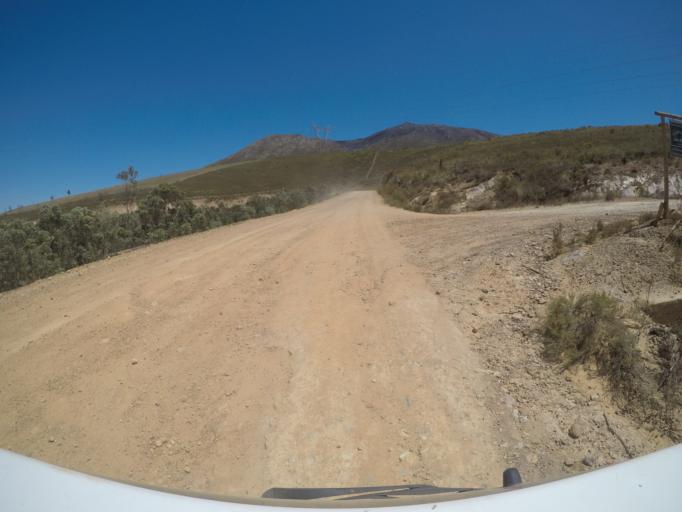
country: ZA
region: Western Cape
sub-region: Overberg District Municipality
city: Grabouw
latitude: -34.2044
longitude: 19.2167
